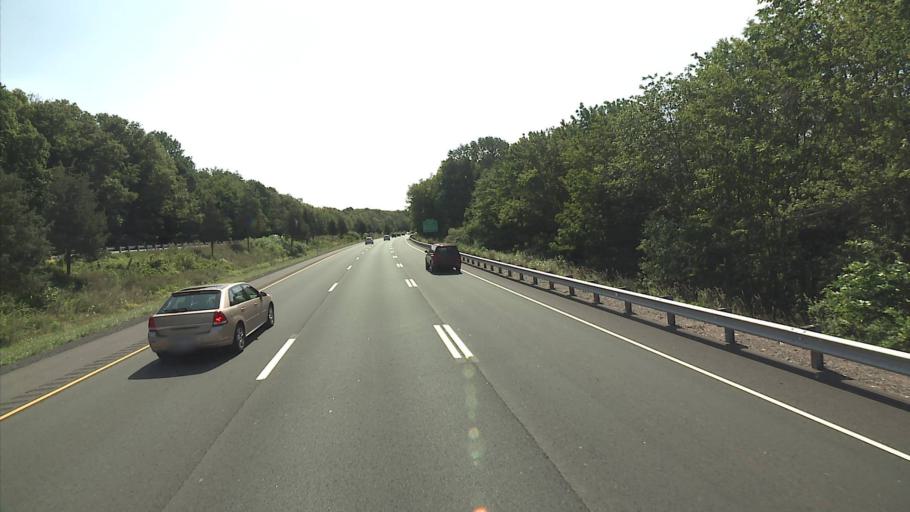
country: US
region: Connecticut
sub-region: Hartford County
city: Terramuggus
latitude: 41.6483
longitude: -72.4752
